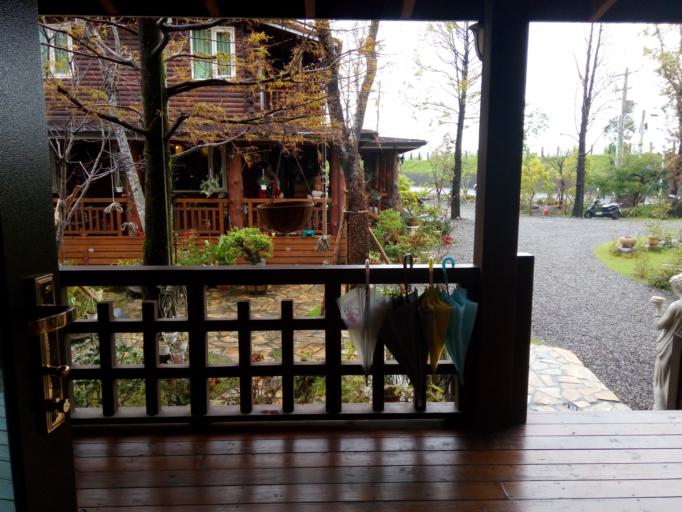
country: TW
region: Taiwan
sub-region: Yilan
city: Yilan
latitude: 24.6749
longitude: 121.7435
